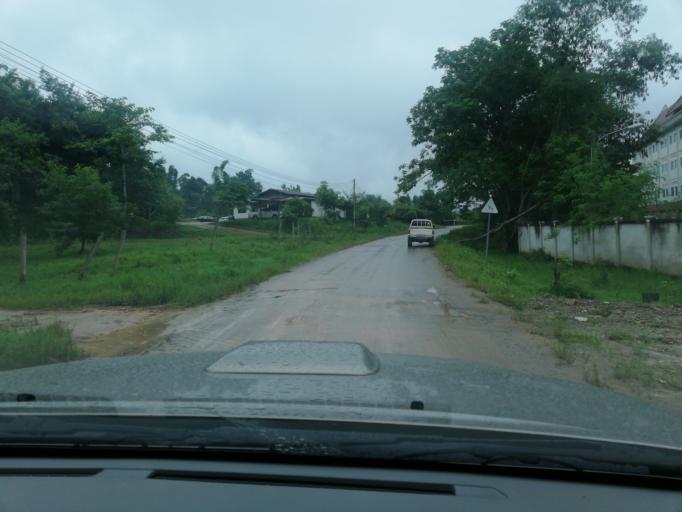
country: LA
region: Loungnamtha
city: Louang Namtha
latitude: 21.0053
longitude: 101.4023
